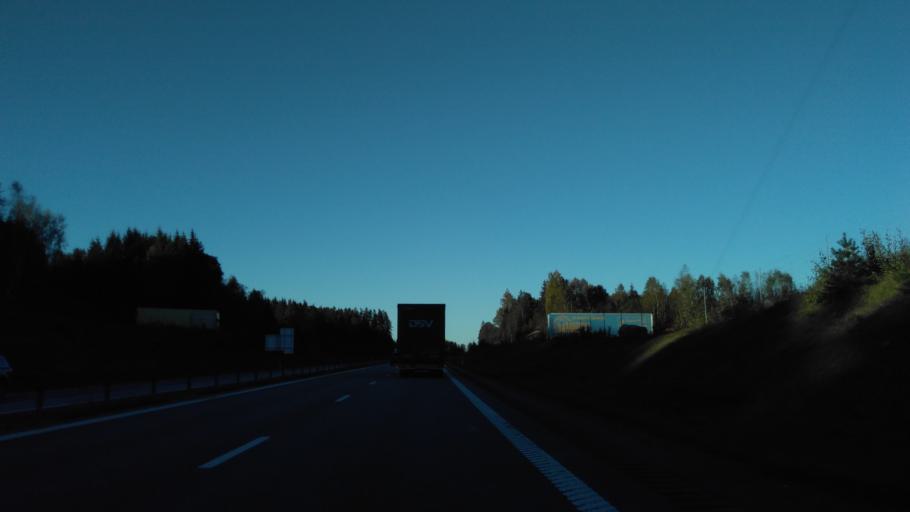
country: SE
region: Vaestra Goetaland
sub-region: Boras Kommun
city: Dalsjofors
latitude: 57.7699
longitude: 13.1135
